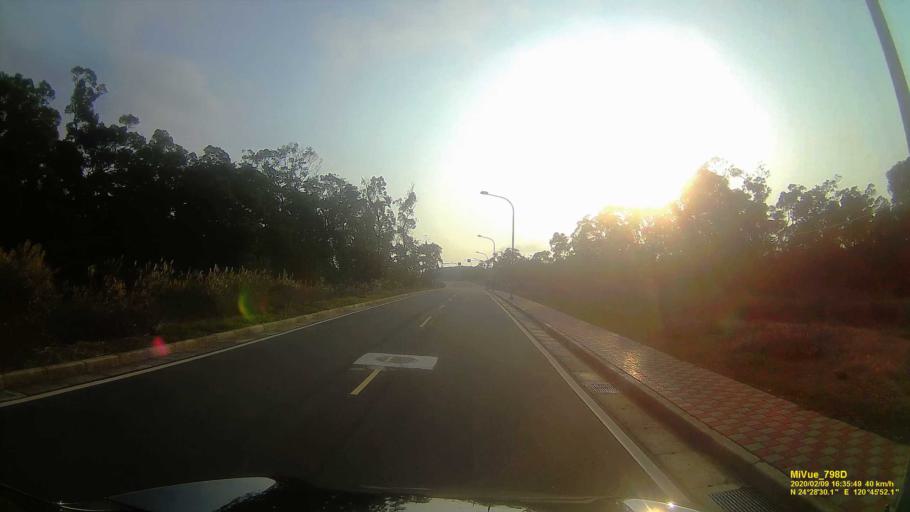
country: TW
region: Taiwan
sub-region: Miaoli
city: Miaoli
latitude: 24.4750
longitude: 120.7644
